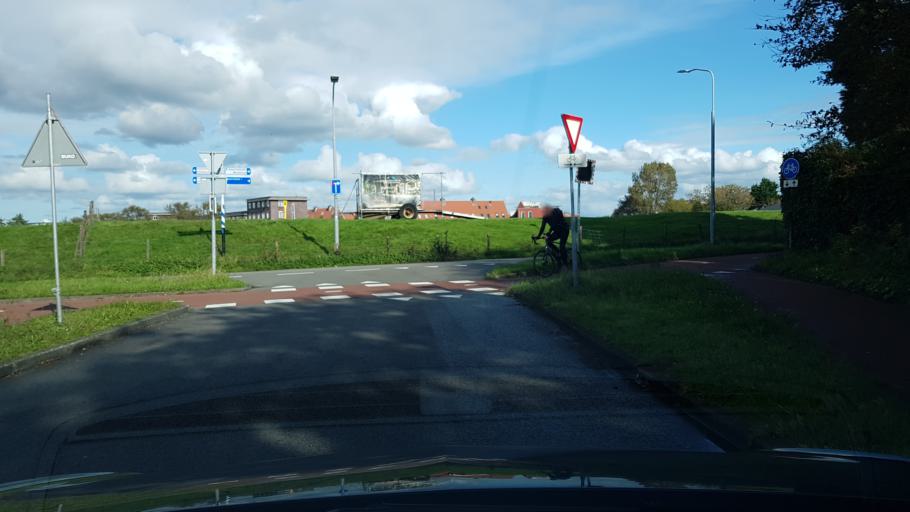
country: NL
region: North Holland
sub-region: Gemeente Velsen
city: Velsen-Zuid
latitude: 52.4244
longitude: 4.6621
